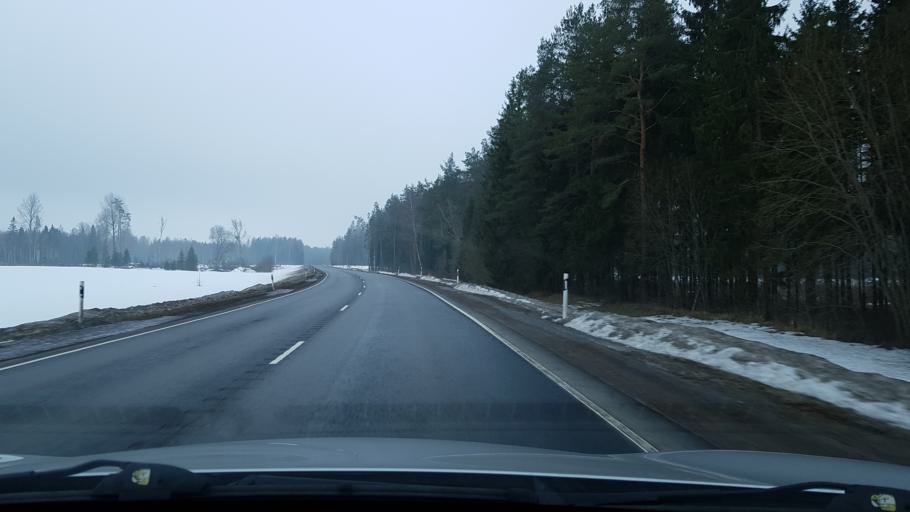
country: EE
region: Valgamaa
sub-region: Valga linn
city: Valga
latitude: 57.8944
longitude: 26.1658
